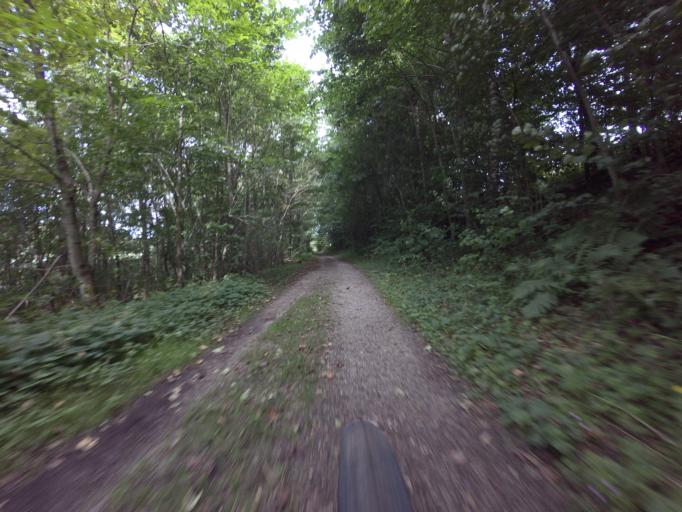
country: DK
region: Central Jutland
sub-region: Syddjurs Kommune
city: Ryomgard
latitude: 56.3832
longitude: 10.5327
